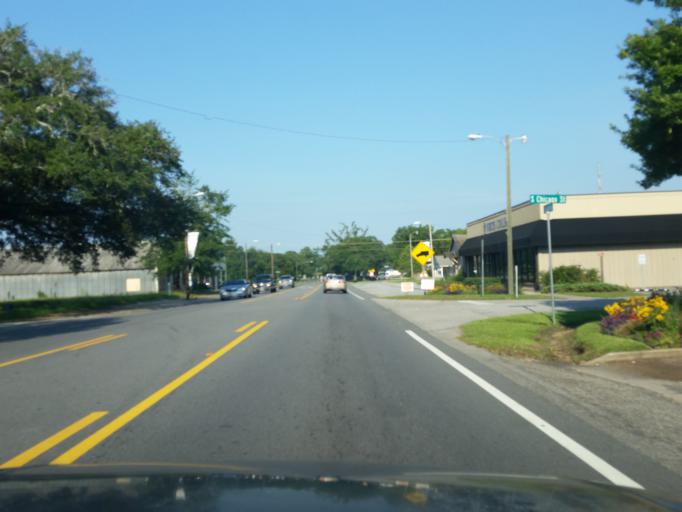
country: US
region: Alabama
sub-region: Baldwin County
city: Foley
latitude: 30.4064
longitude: -87.6824
